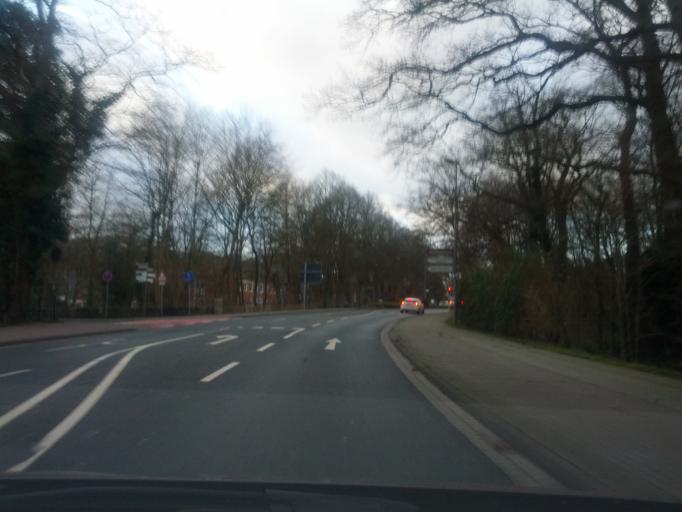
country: DE
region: Lower Saxony
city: Rotenburg
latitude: 53.1102
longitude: 9.3945
